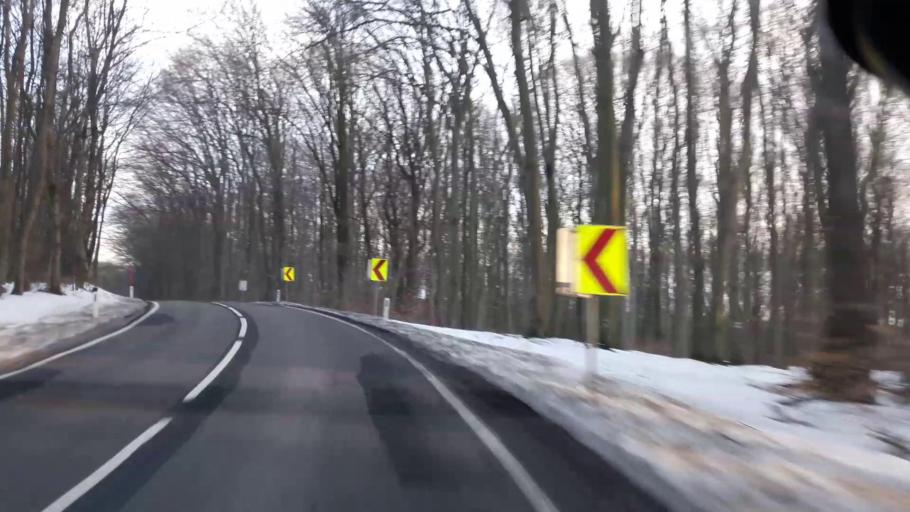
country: AT
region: Lower Austria
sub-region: Politischer Bezirk Wien-Umgebung
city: Mauerbach
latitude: 48.2766
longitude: 16.1780
